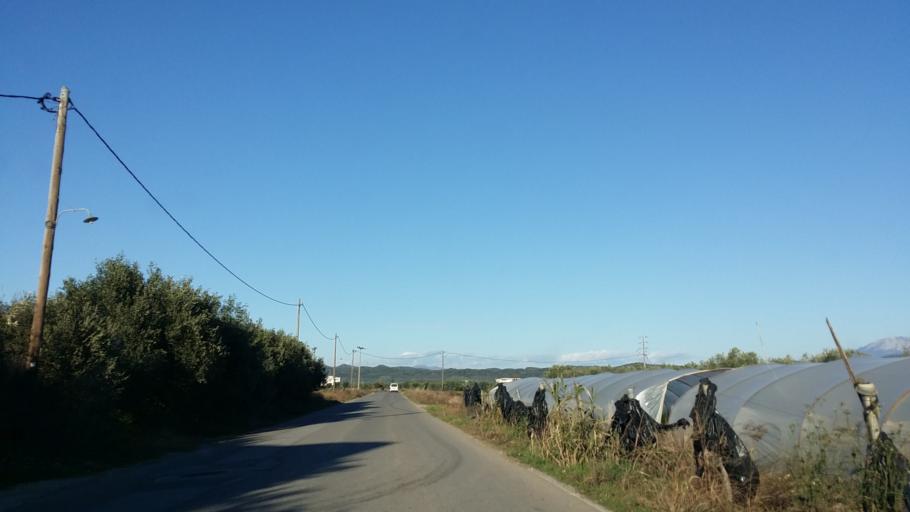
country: GR
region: West Greece
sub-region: Nomos Aitolias kai Akarnanias
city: Lepenou
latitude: 38.6628
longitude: 21.2941
